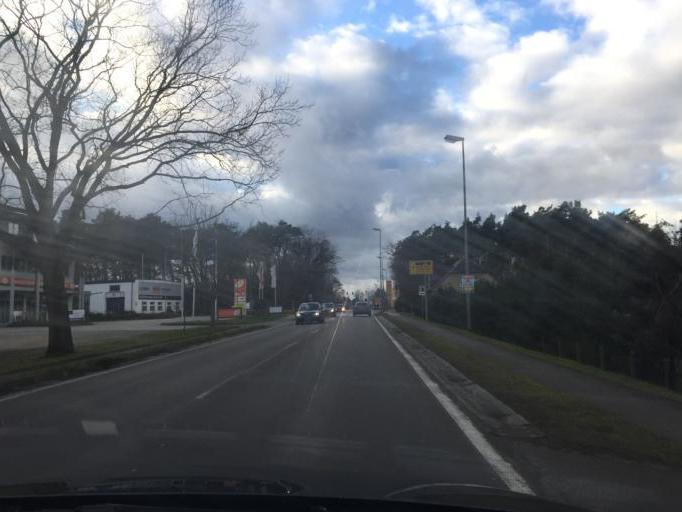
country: DE
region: Brandenburg
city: Kolkwitz
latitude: 51.7500
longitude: 14.2640
